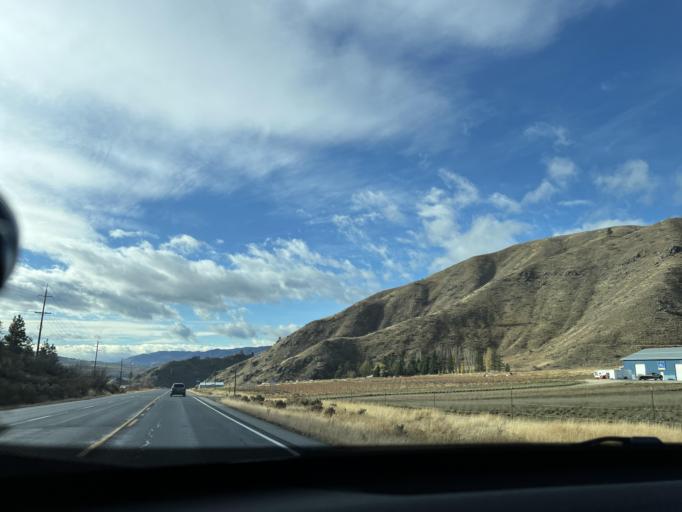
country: US
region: Washington
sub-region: Chelan County
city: Manson
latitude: 47.7879
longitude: -120.1359
